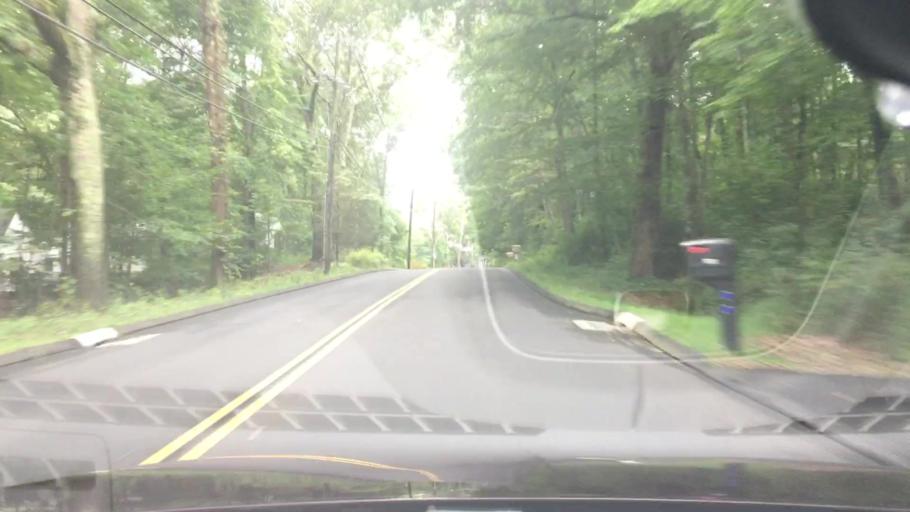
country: US
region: Connecticut
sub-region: New Haven County
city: Madison
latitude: 41.3183
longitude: -72.5943
